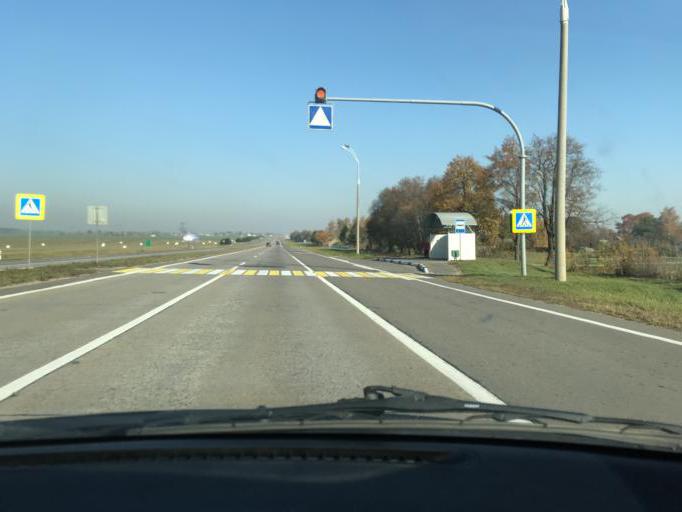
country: BY
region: Minsk
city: Samakhvalavichy
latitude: 53.6559
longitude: 27.4761
